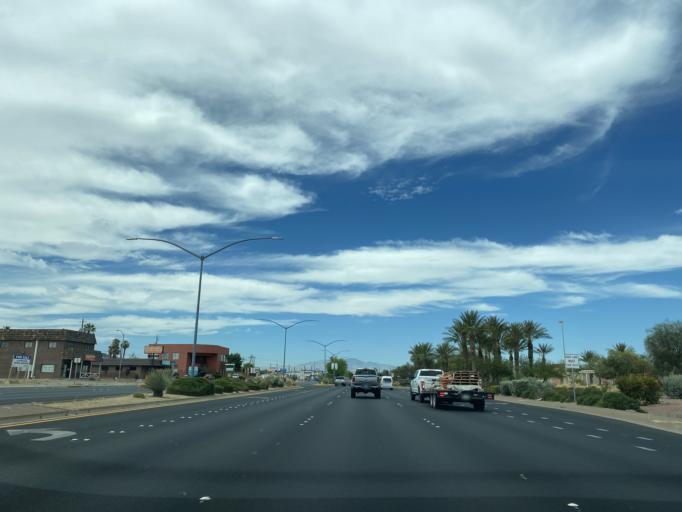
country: US
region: Nevada
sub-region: Clark County
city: Henderson
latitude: 36.0365
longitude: -114.9913
